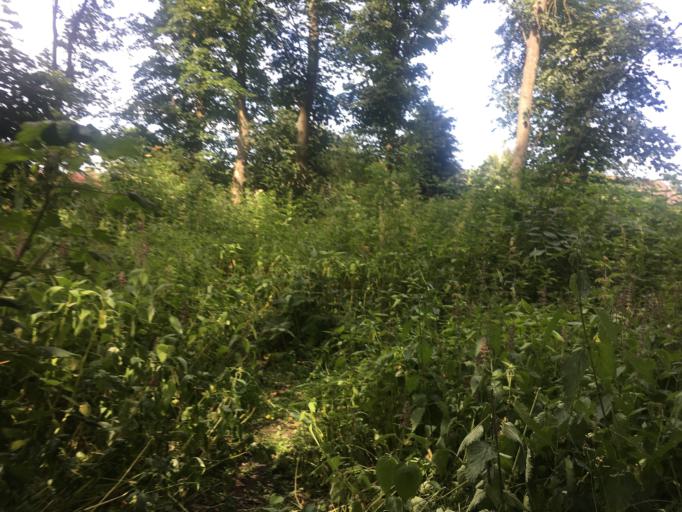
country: GB
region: England
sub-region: Sunderland
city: Washington
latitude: 54.8780
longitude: -1.5317
